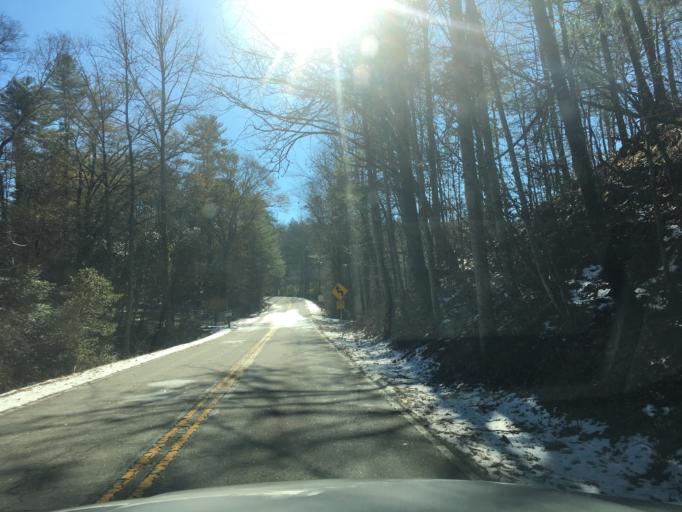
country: US
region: South Carolina
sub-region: Greenville County
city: Slater-Marietta
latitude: 35.0666
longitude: -82.6184
